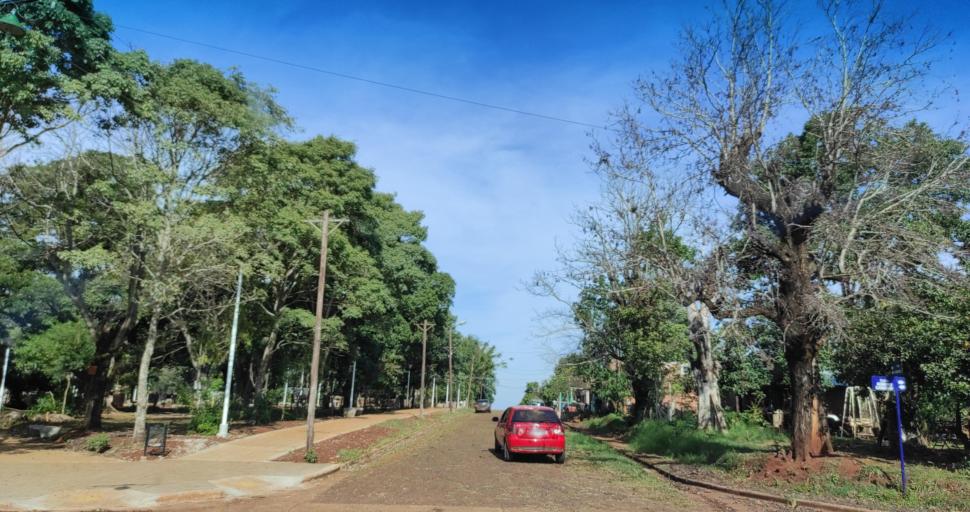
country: AR
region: Misiones
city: Garupa
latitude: -27.4832
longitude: -55.8304
